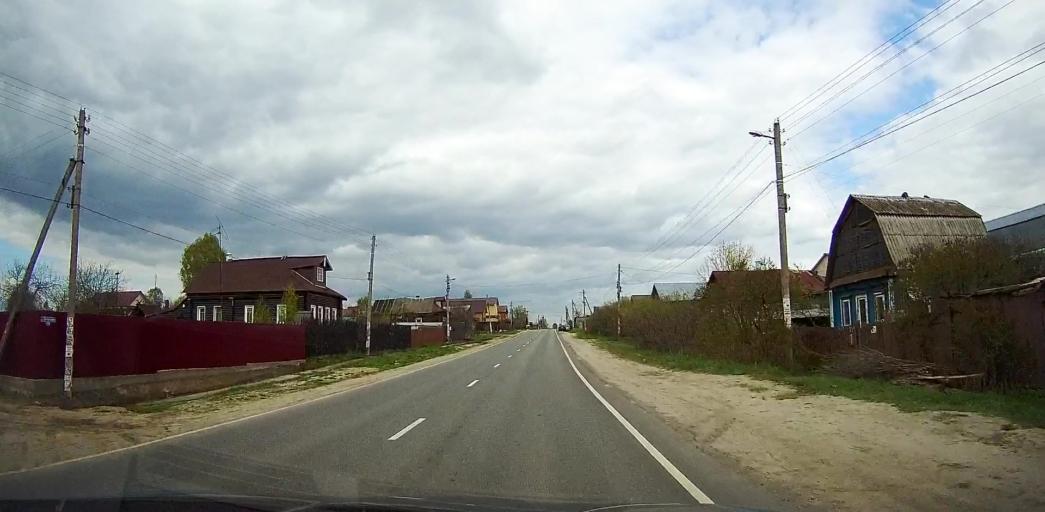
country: RU
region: Moskovskaya
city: Ashitkovo
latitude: 55.4515
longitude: 38.5936
